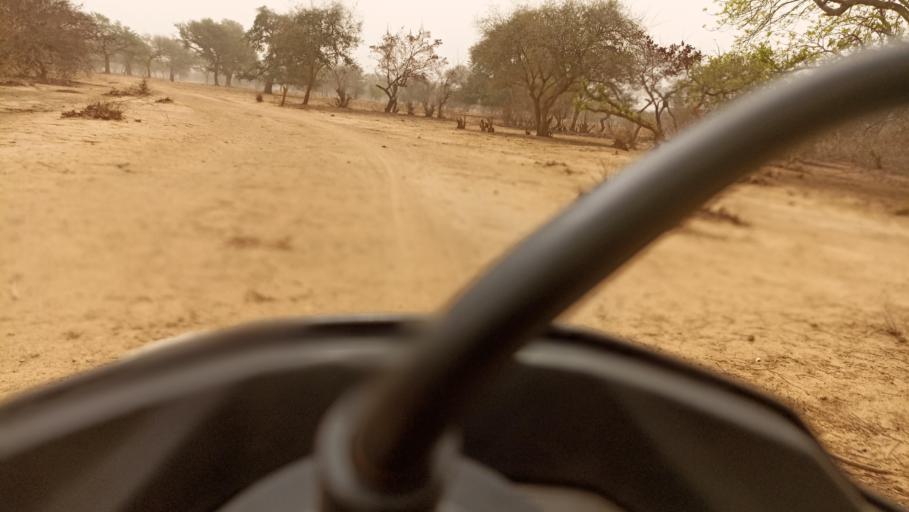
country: BF
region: Nord
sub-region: Province du Zondoma
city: Gourcy
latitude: 13.2498
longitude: -2.6020
